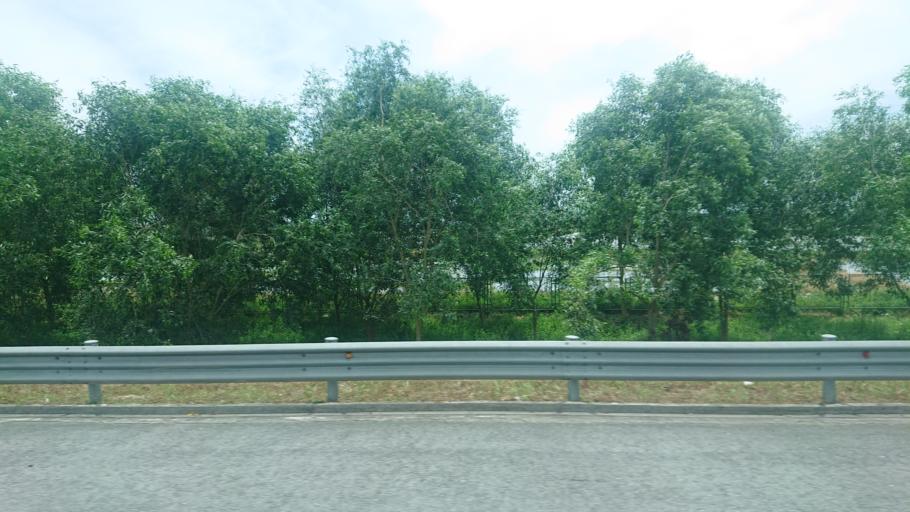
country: VN
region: Hai Phong
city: An Lao
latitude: 20.7988
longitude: 106.5378
